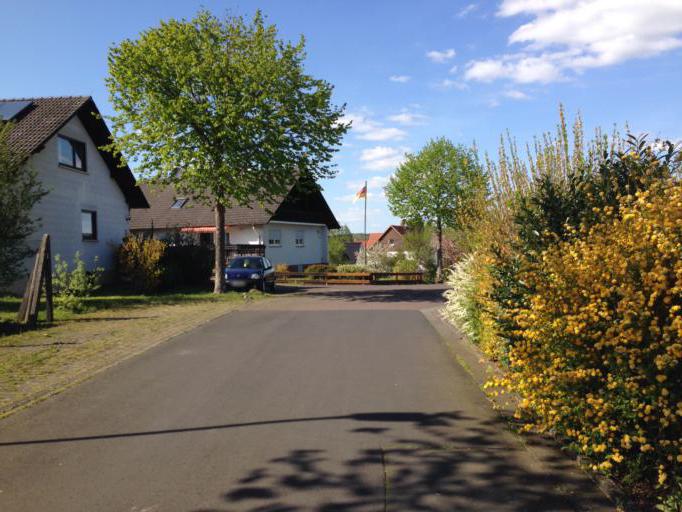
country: DE
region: Hesse
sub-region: Regierungsbezirk Giessen
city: Grunberg
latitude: 50.5568
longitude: 8.9074
